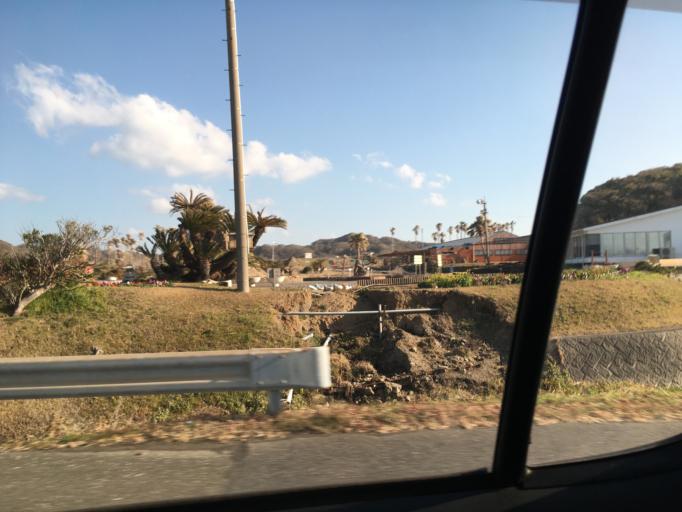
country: JP
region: Chiba
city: Tateyama
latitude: 34.9463
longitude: 139.8133
